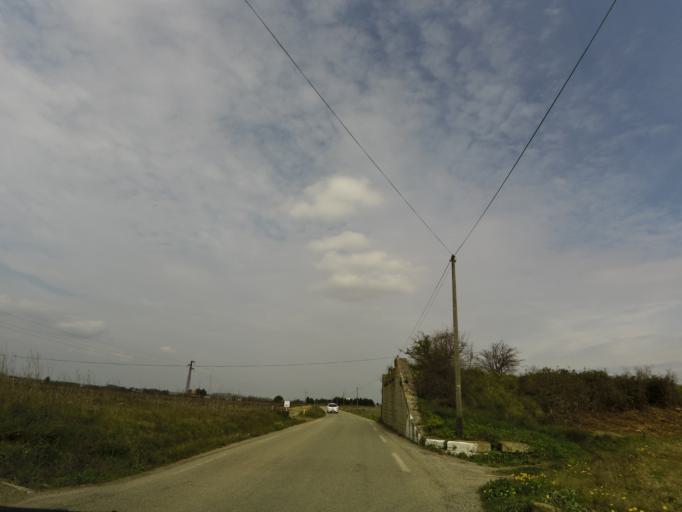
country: FR
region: Languedoc-Roussillon
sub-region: Departement de l'Herault
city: Marsillargues
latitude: 43.6697
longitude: 4.1844
